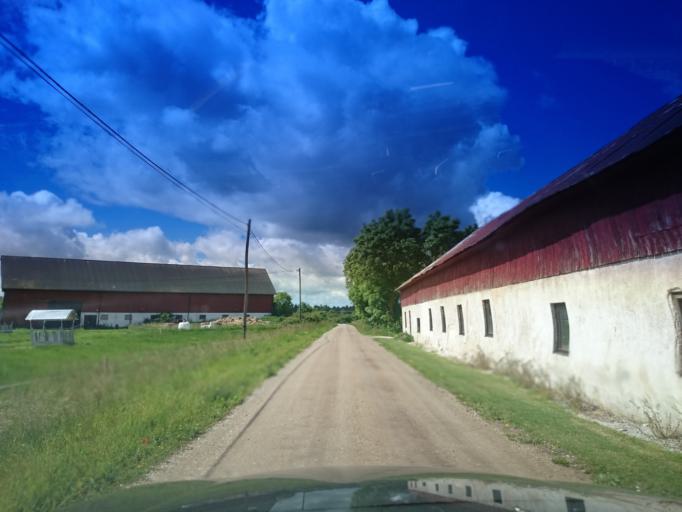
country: SE
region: Gotland
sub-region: Gotland
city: Hemse
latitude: 57.3385
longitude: 18.6151
